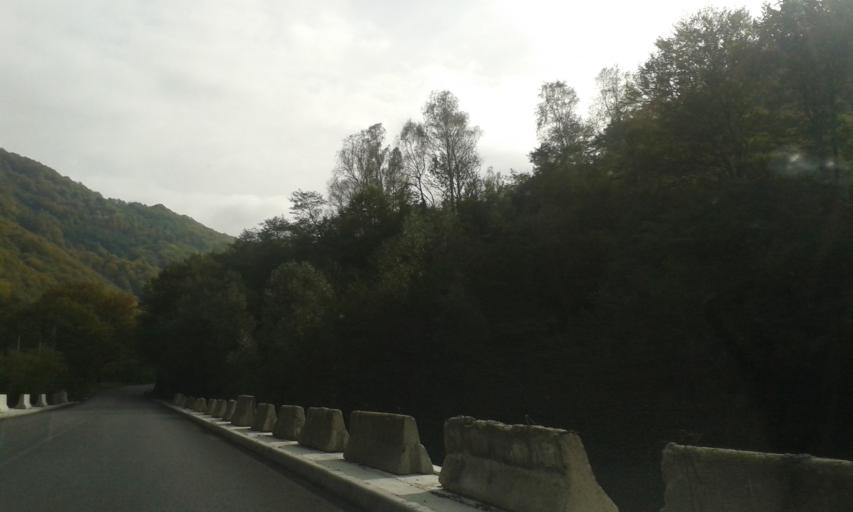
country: RO
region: Gorj
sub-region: Comuna Bumbesti-Jiu
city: Bumbesti-Jiu
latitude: 45.2709
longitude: 23.3828
